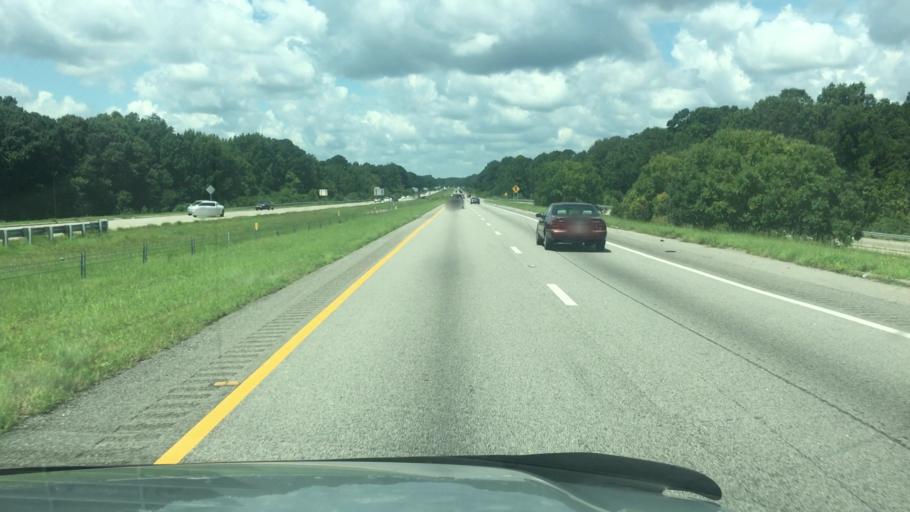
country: US
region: South Carolina
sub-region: Kershaw County
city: Camden
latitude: 34.2171
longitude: -80.5935
